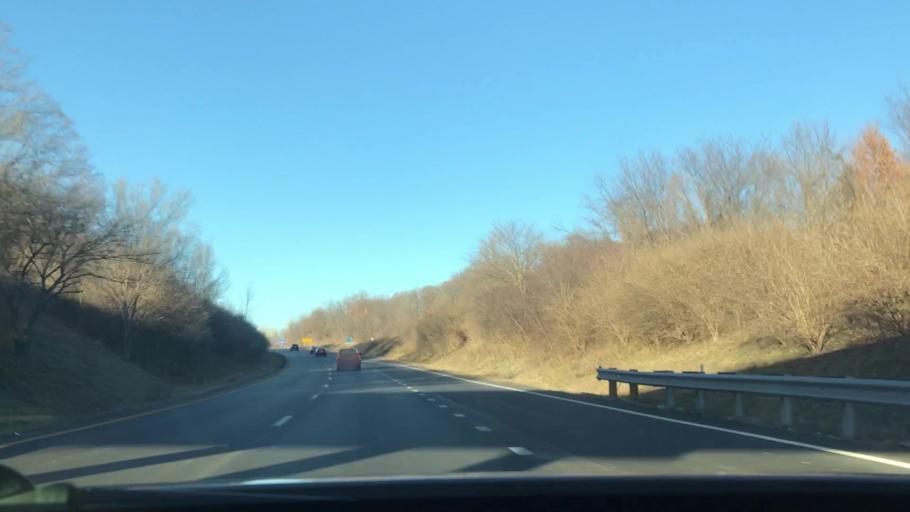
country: US
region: Missouri
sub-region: Platte County
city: Riverside
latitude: 39.1842
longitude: -94.5909
